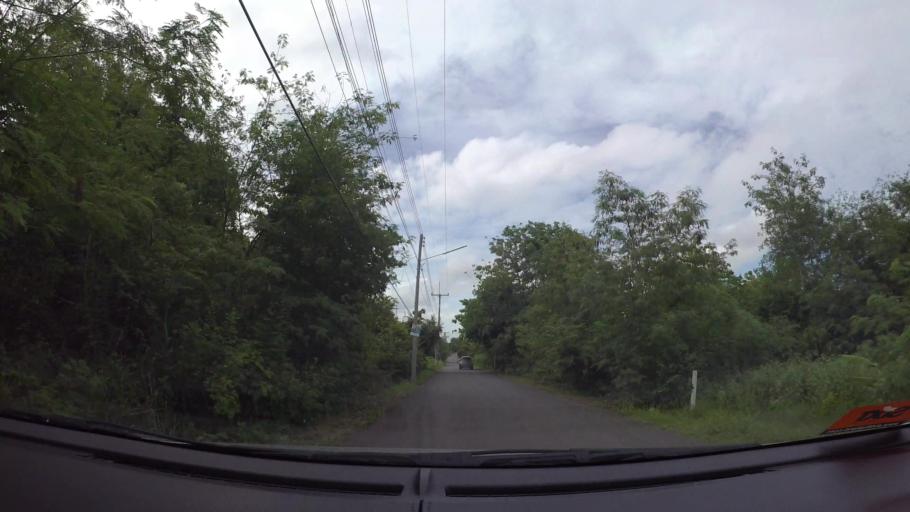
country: TH
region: Chon Buri
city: Sattahip
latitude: 12.7188
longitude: 100.8993
